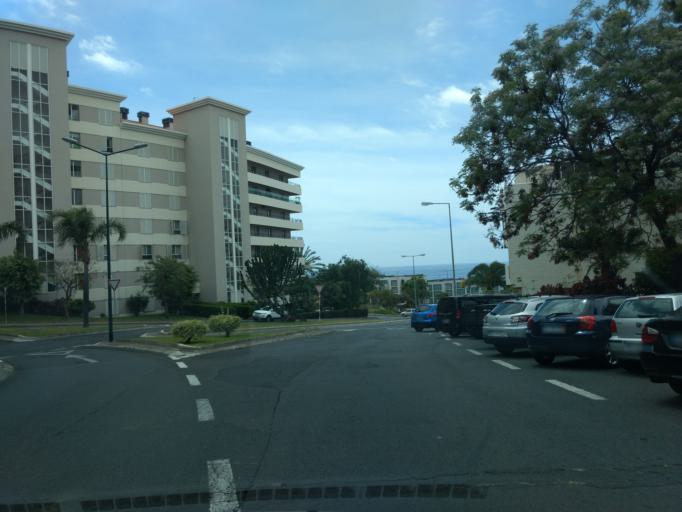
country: PT
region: Madeira
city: Camara de Lobos
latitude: 32.6404
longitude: -16.9451
